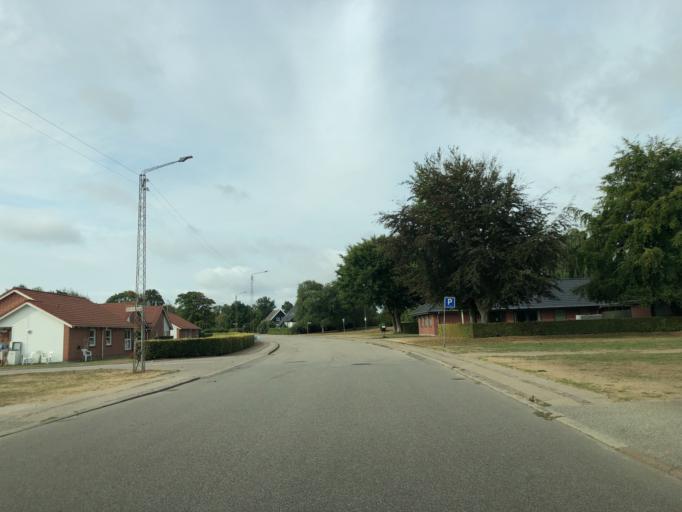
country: DK
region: Central Jutland
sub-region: Ringkobing-Skjern Kommune
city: Tarm
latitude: 55.9070
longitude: 8.5163
